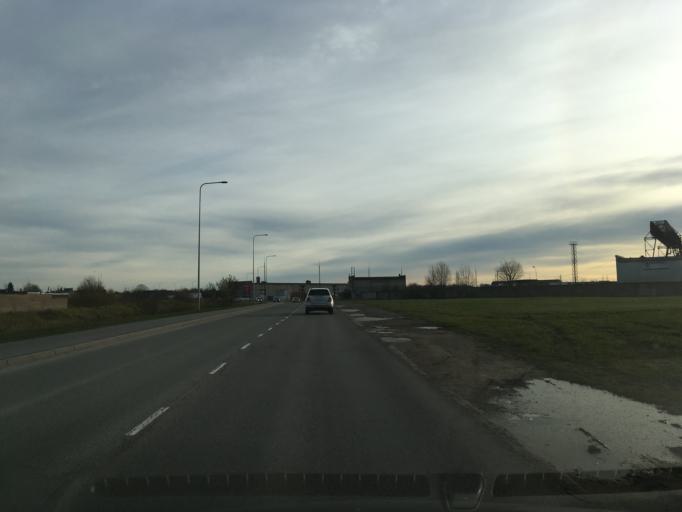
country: EE
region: Ida-Virumaa
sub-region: Narva linn
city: Narva
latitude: 59.3643
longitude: 28.1711
